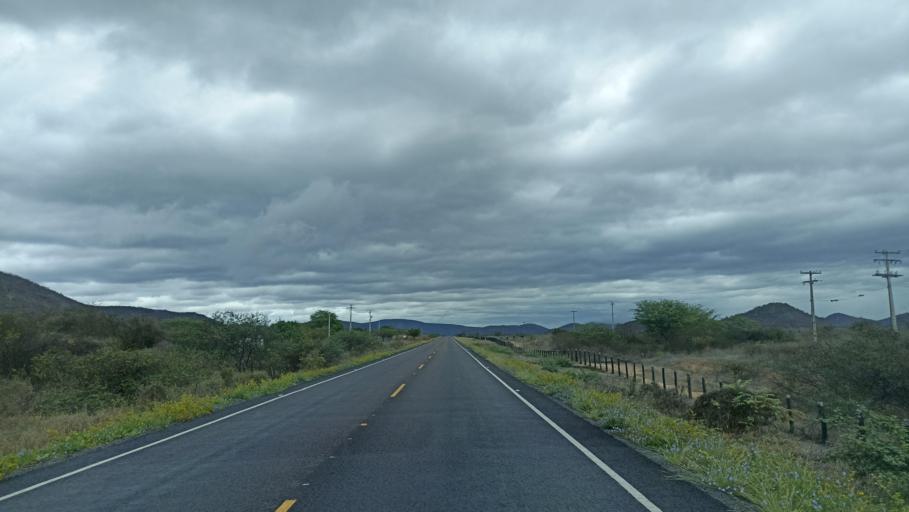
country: BR
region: Bahia
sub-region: Iacu
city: Iacu
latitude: -12.8976
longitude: -40.4005
